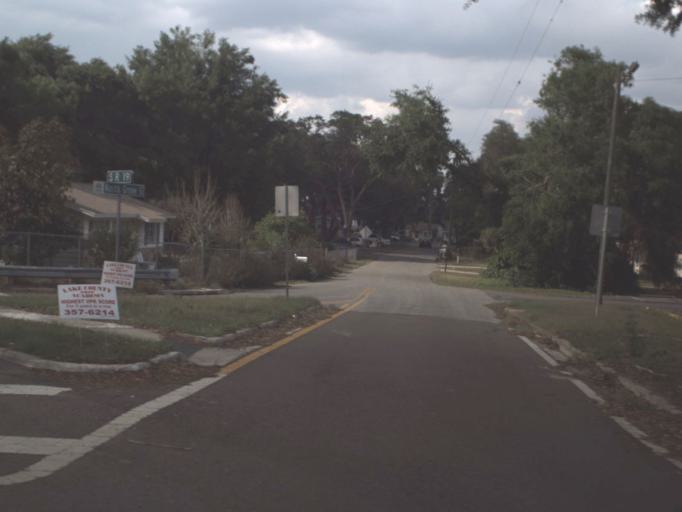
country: US
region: Florida
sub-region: Lake County
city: Eustis
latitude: 28.8618
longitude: -81.6840
